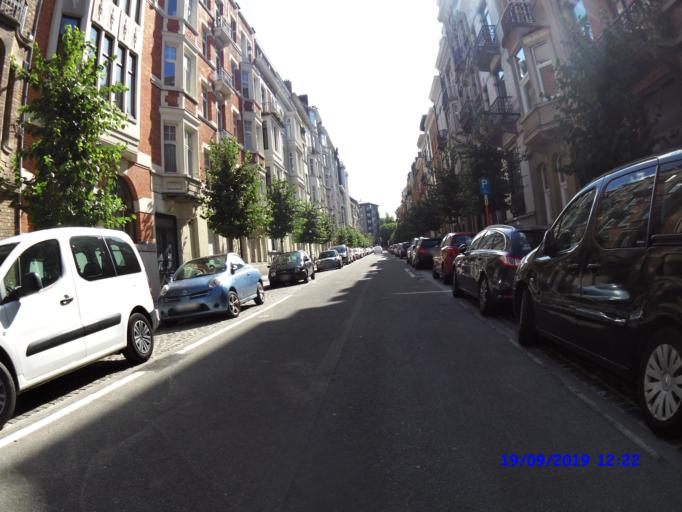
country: BE
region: Brussels Capital
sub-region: Bruxelles-Capitale
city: Brussels
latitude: 50.8284
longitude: 4.3781
